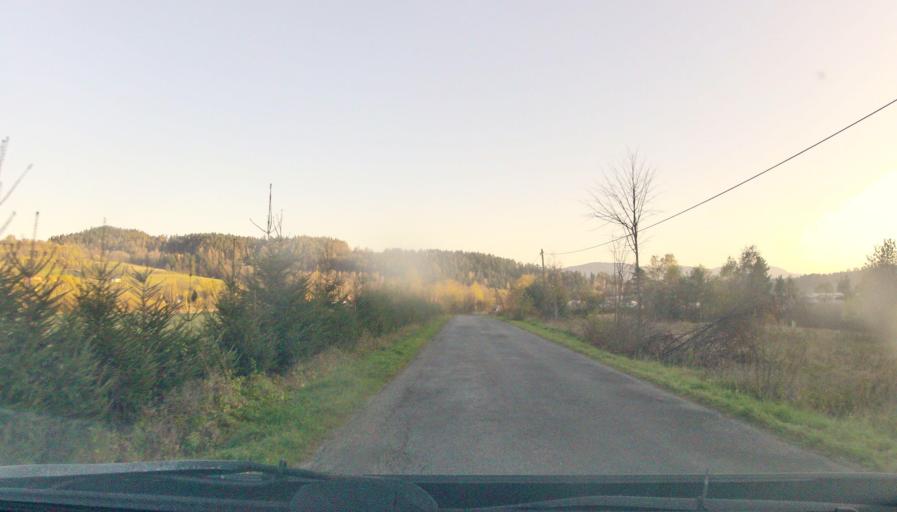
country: PL
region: Lesser Poland Voivodeship
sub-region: Powiat suski
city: Krzeszow
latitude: 49.7511
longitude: 19.4627
